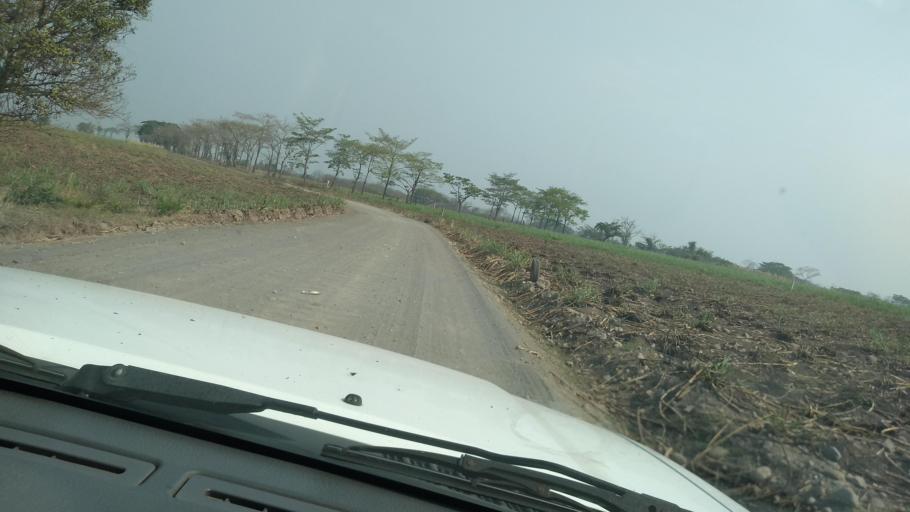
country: MX
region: Veracruz
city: Tezonapa
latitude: 18.6283
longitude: -96.6105
